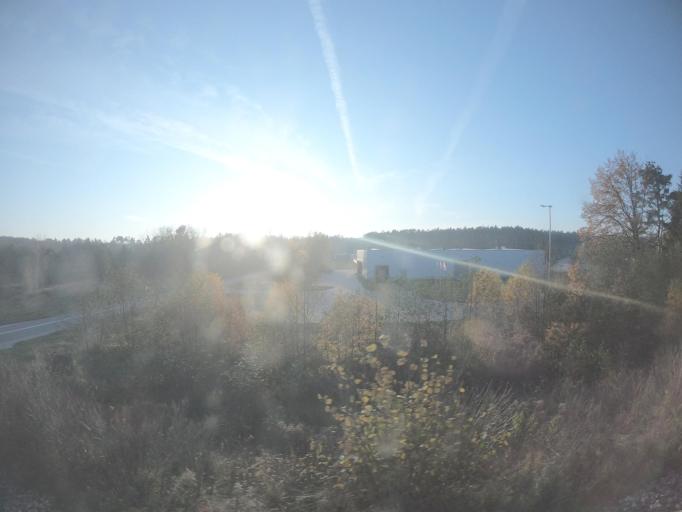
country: PL
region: Lubusz
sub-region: Powiat slubicki
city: Rzepin
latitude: 52.3380
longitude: 14.8315
